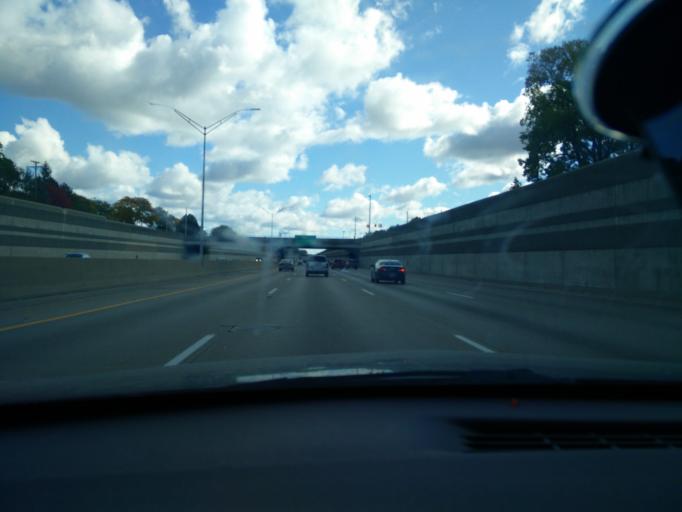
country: US
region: Michigan
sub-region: Oakland County
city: Huntington Woods
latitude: 42.4746
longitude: -83.1749
